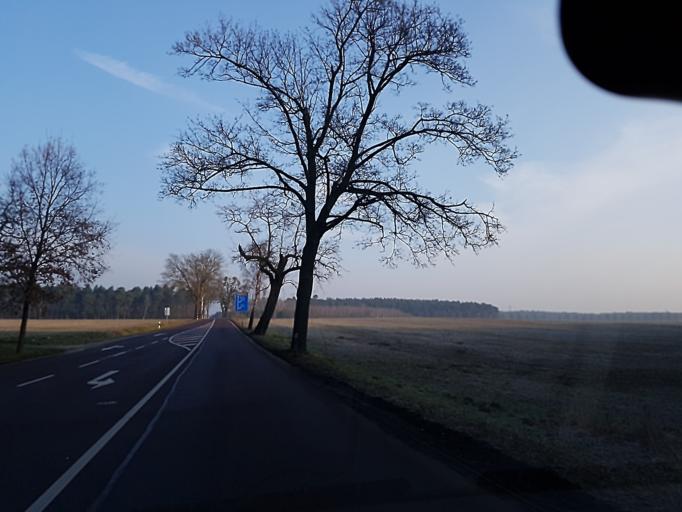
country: DE
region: Saxony-Anhalt
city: Coswig
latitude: 51.9553
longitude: 12.4635
